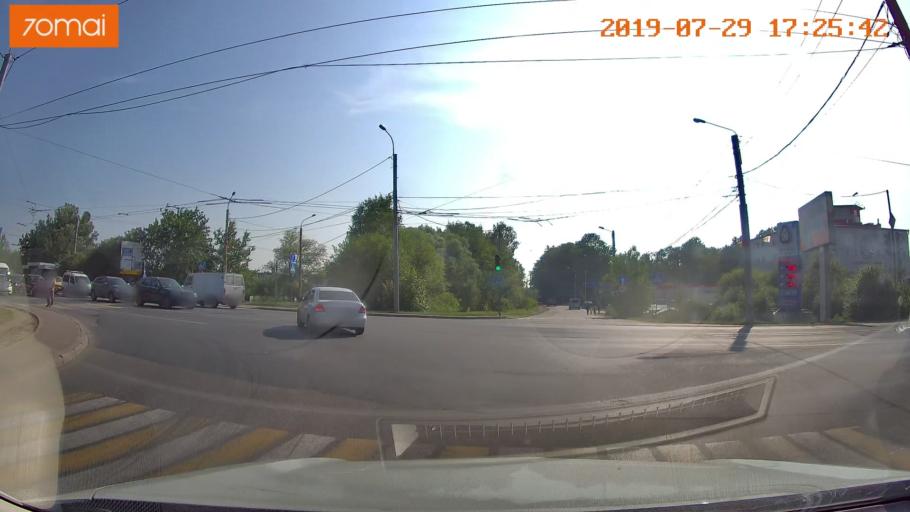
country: RU
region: Kaliningrad
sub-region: Gorod Kaliningrad
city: Kaliningrad
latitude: 54.7608
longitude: 20.4427
